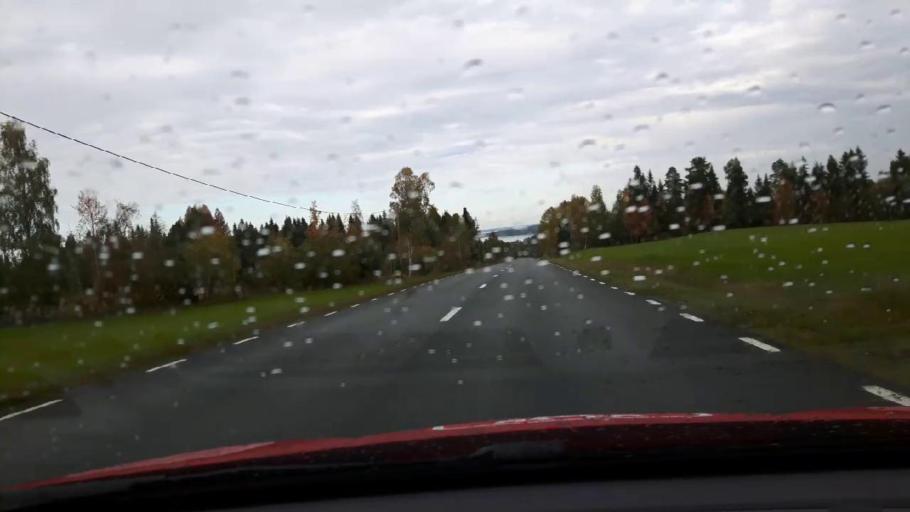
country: SE
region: Jaemtland
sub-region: Krokoms Kommun
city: Krokom
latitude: 63.1165
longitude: 14.2932
